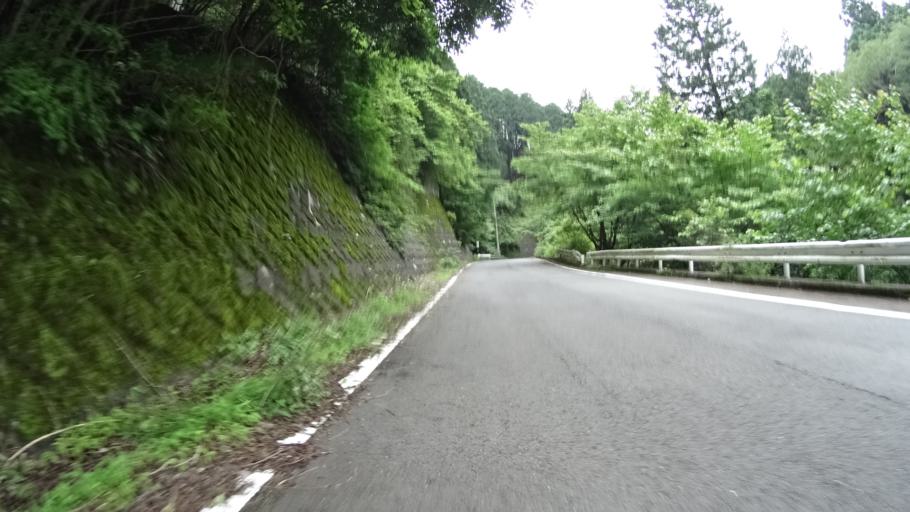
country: JP
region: Kanagawa
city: Hadano
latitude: 35.4499
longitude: 139.2135
